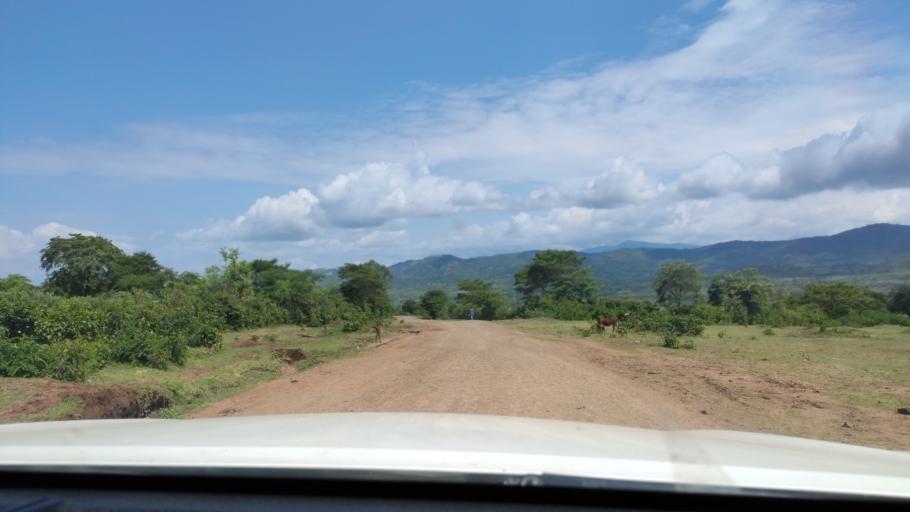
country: ET
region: Southern Nations, Nationalities, and People's Region
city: Felege Neway
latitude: 6.3653
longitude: 36.9841
